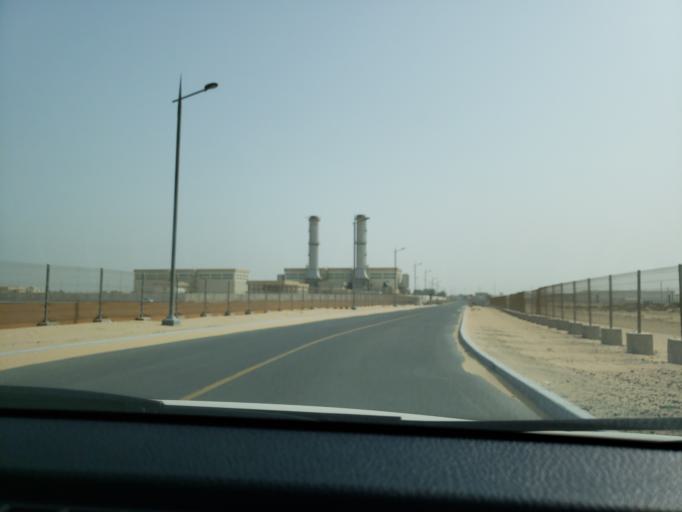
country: AE
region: Ajman
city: Ajman
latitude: 25.4414
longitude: 55.4764
